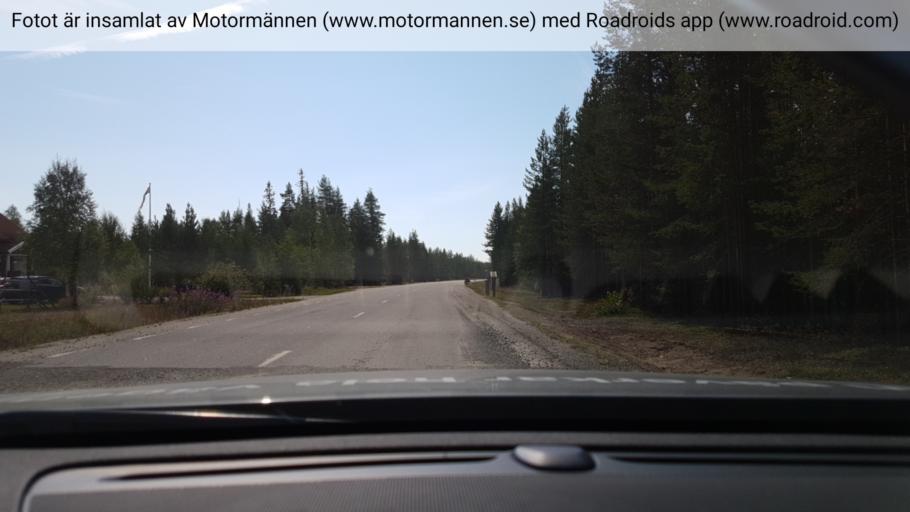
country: SE
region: Vaesterbotten
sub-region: Norsjo Kommun
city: Norsjoe
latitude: 64.6059
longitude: 19.2969
